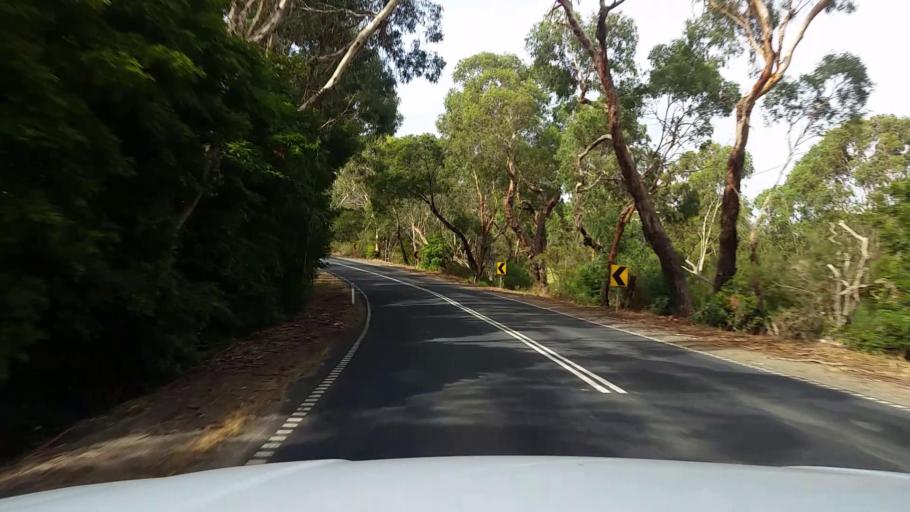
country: AU
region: Victoria
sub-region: Mornington Peninsula
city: Mount Martha
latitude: -38.2870
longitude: 145.0713
